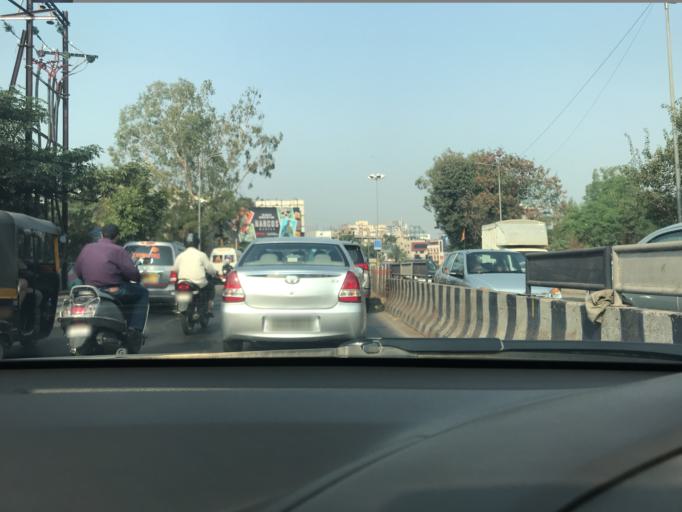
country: IN
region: Maharashtra
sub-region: Pune Division
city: Khadki
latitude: 18.5507
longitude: 73.8056
